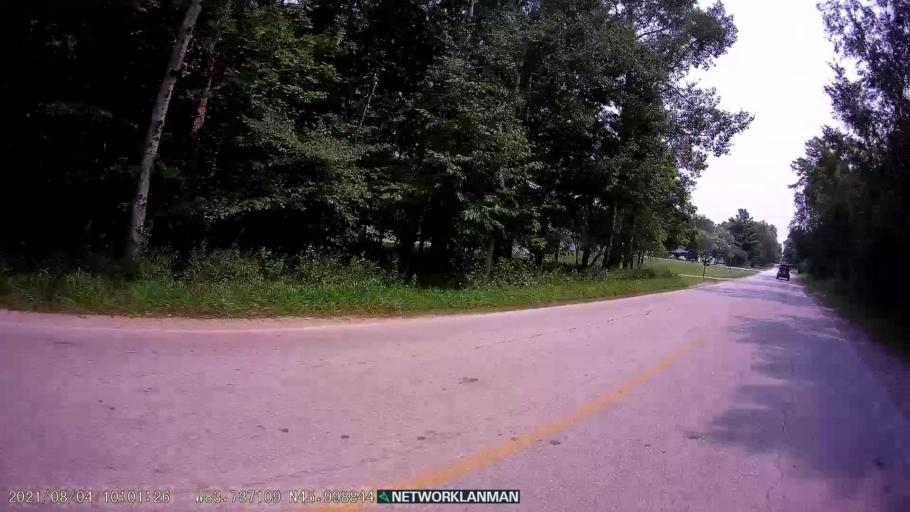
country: CA
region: Ontario
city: Thessalon
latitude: 45.9988
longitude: -83.7369
